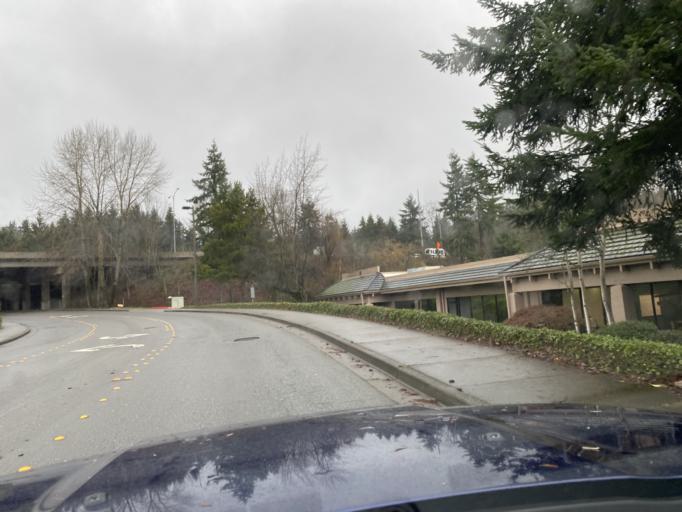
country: US
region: Washington
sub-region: King County
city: Bellevue
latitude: 47.6289
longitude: -122.1667
